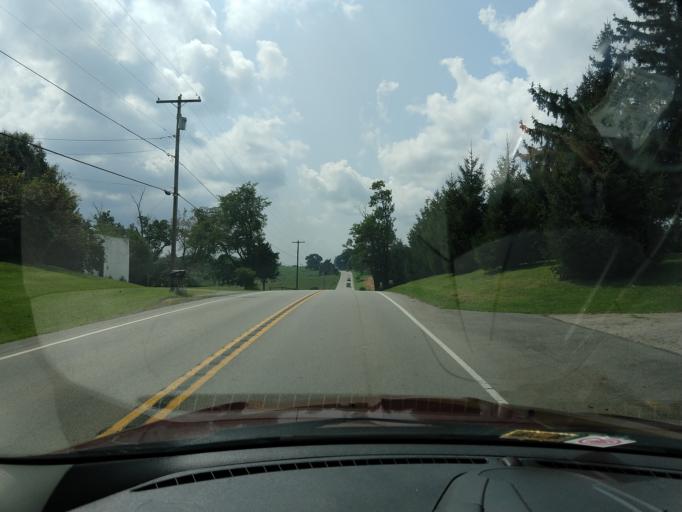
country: US
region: Pennsylvania
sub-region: Washington County
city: Ellsworth
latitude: 40.1869
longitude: -80.0581
